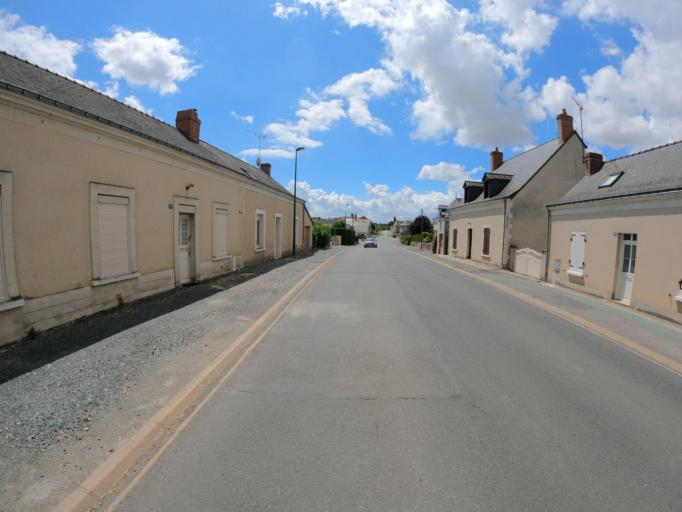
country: FR
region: Pays de la Loire
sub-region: Departement de Maine-et-Loire
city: Mire
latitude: 47.7593
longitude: -0.4890
